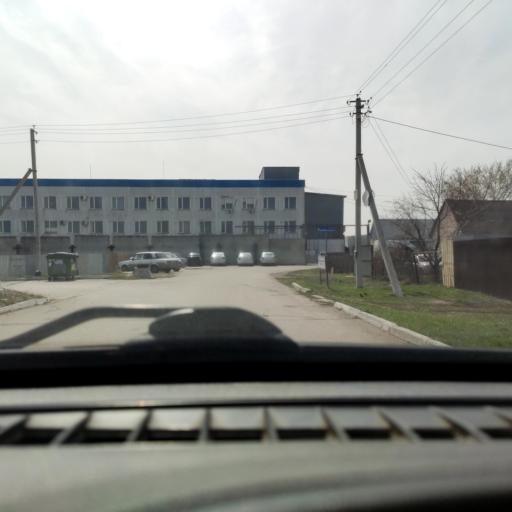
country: RU
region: Samara
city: Tol'yatti
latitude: 53.5743
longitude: 49.3047
